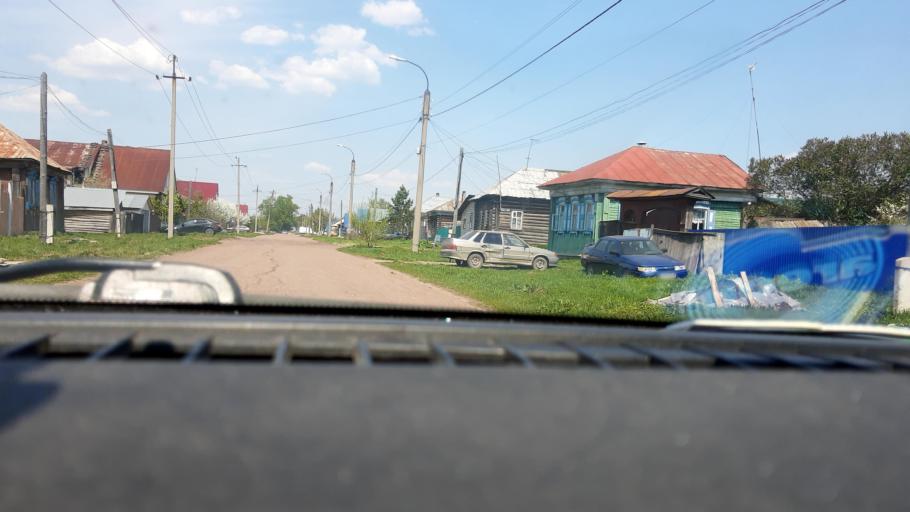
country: RU
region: Bashkortostan
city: Blagoveshchensk
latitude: 55.0236
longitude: 55.9837
